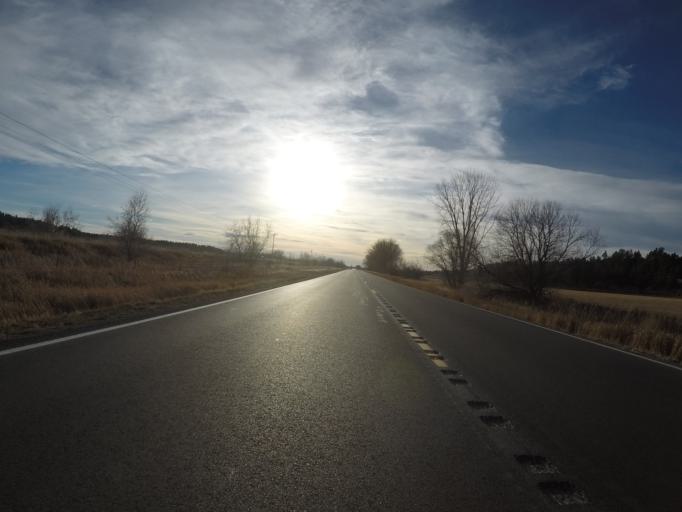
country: US
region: Montana
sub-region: Musselshell County
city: Roundup
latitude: 46.3855
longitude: -108.6229
